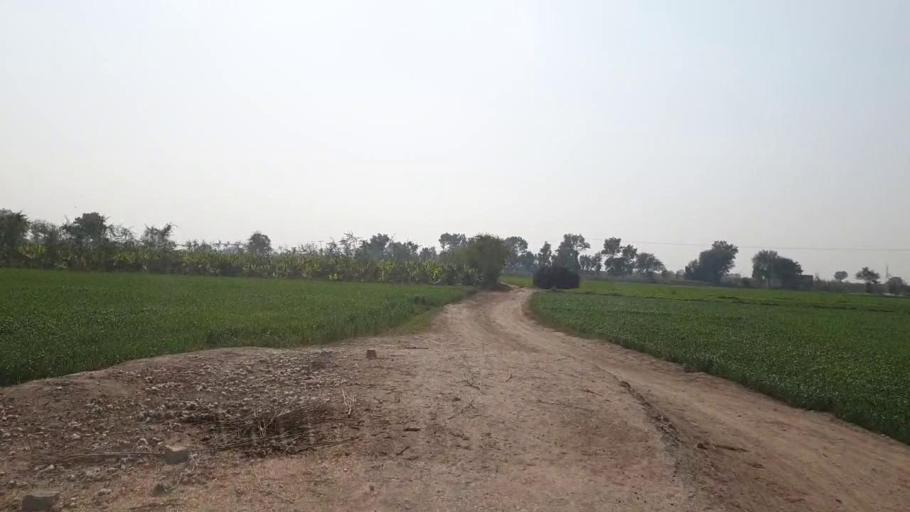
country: PK
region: Sindh
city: Bhit Shah
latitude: 25.7467
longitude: 68.5160
